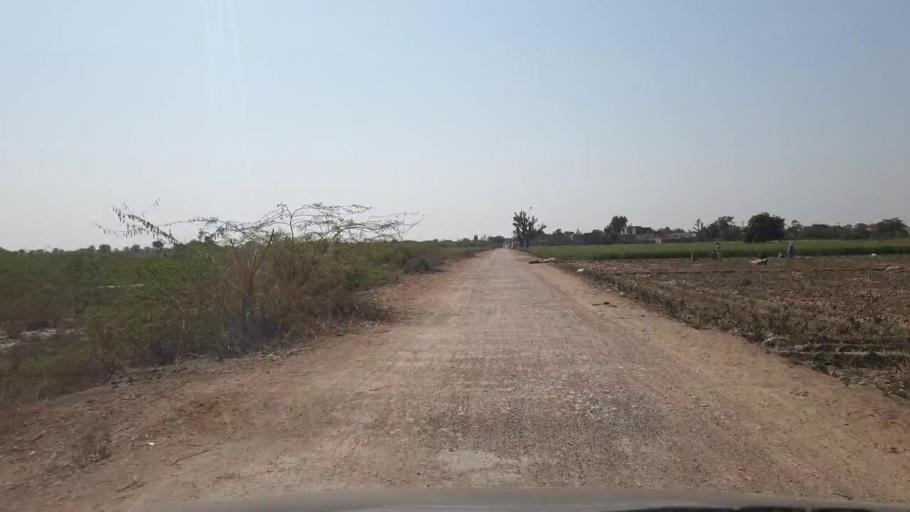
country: PK
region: Sindh
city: Digri
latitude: 25.1852
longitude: 69.2172
